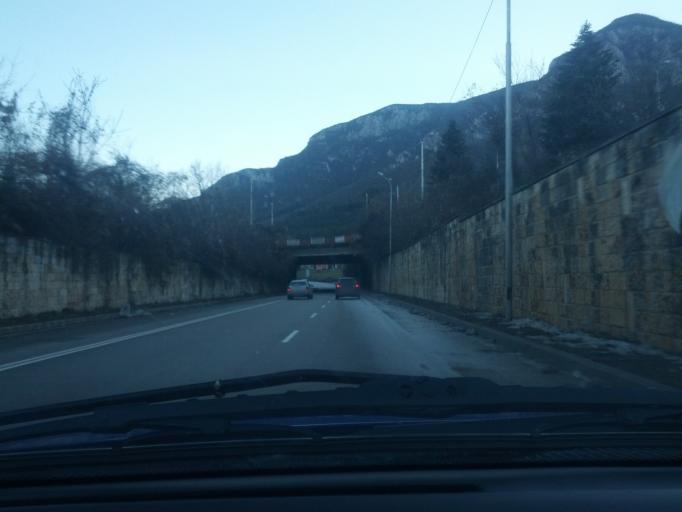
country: BG
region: Vratsa
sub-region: Obshtina Vratsa
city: Vratsa
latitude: 43.1914
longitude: 23.5753
